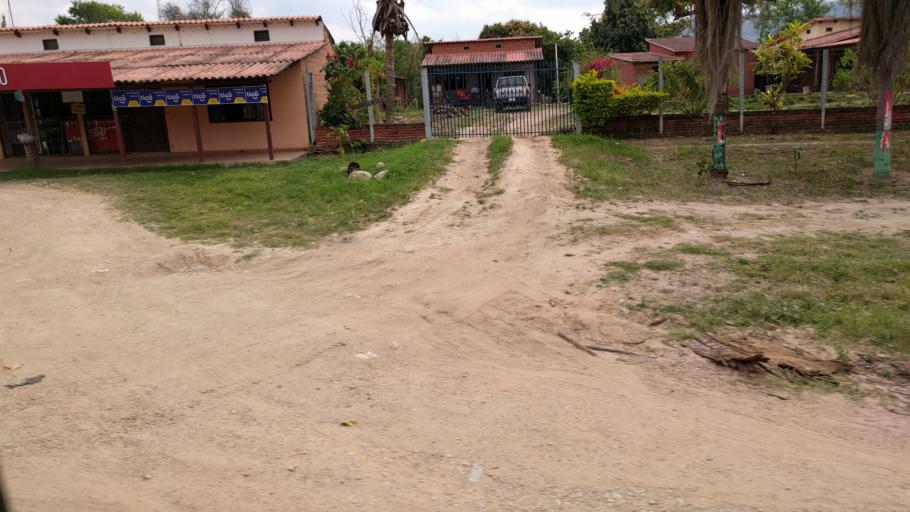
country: BO
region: Santa Cruz
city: Jorochito
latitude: -18.1118
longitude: -63.4588
